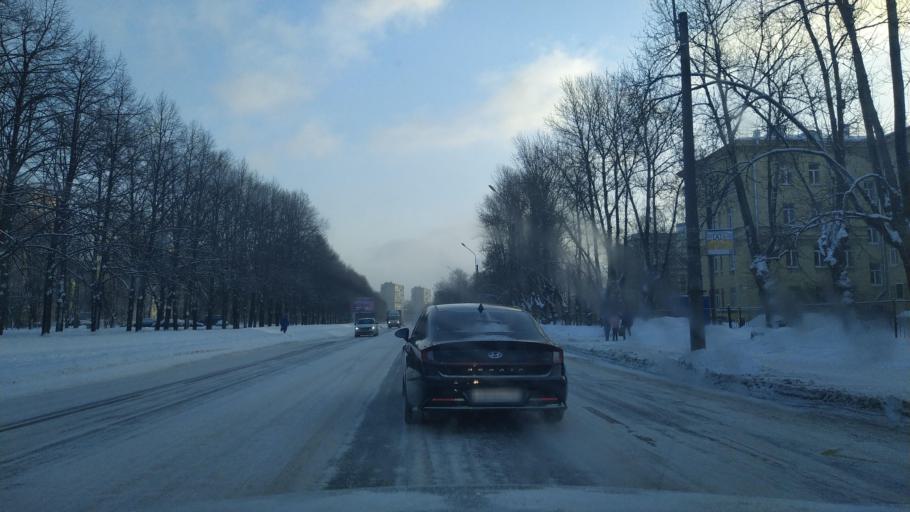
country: RU
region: Leningrad
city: Kalininskiy
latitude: 59.9663
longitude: 30.4006
